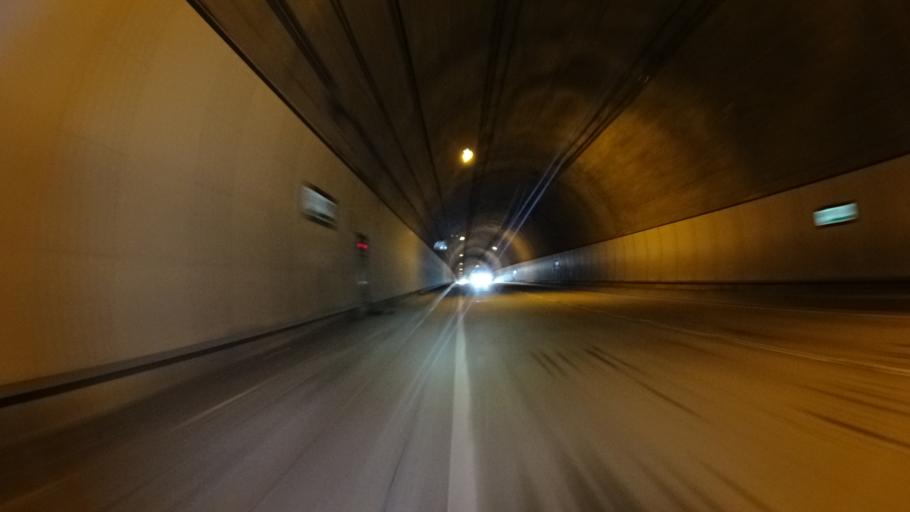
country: JP
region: Yamanashi
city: Uenohara
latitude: 35.6937
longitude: 139.1039
